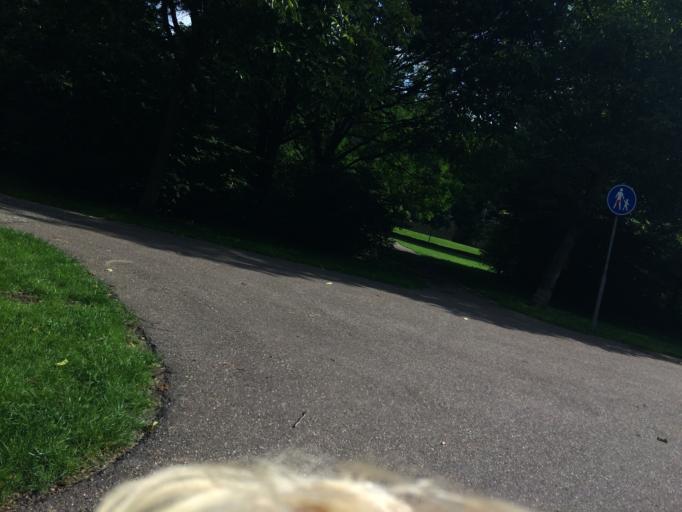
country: NL
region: North Brabant
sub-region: Gemeente 's-Hertogenbosch
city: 's-Hertogenbosch
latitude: 51.7204
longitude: 5.3067
